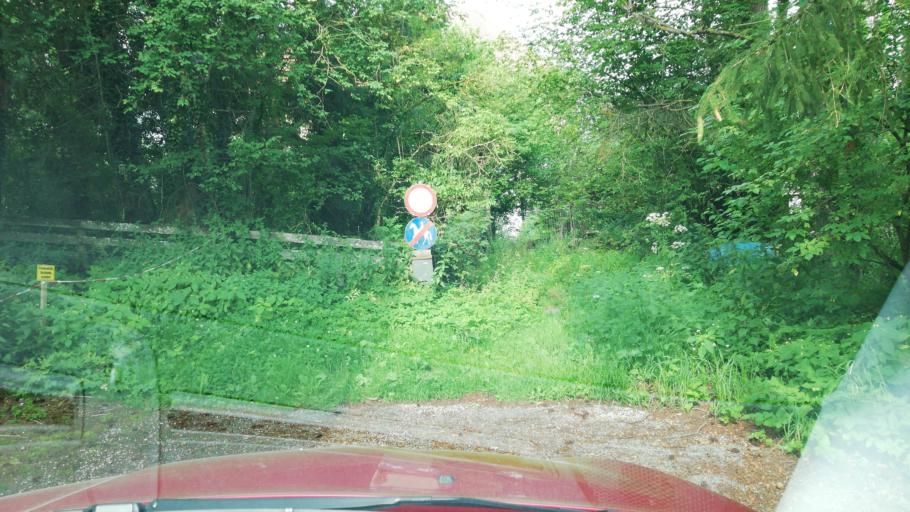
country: AT
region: Upper Austria
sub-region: Politischer Bezirk Rohrbach
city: Kleinzell im Muehlkreis
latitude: 48.5020
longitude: 14.0136
